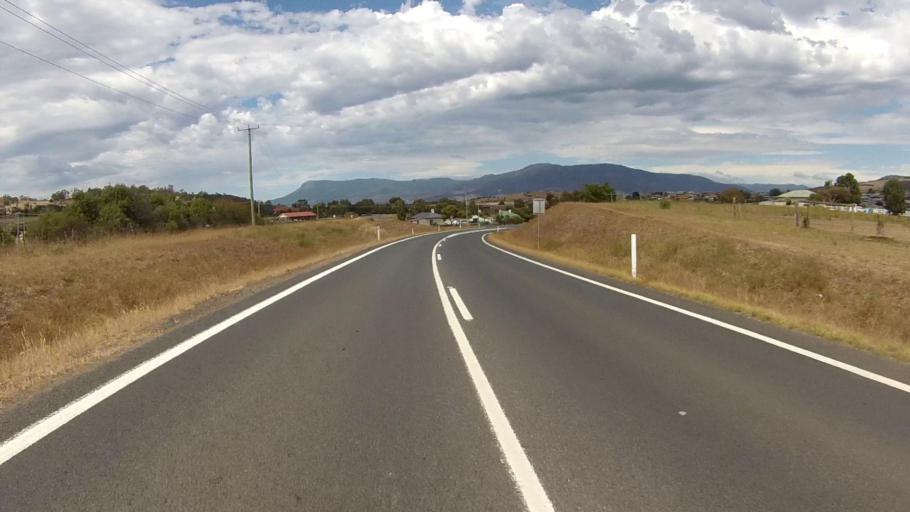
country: AU
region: Tasmania
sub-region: Brighton
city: Bridgewater
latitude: -42.6995
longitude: 147.2690
